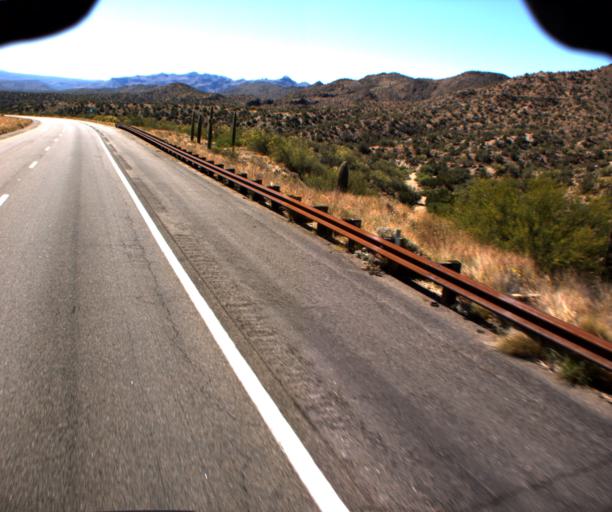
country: US
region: Arizona
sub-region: Yavapai County
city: Bagdad
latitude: 34.4338
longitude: -113.2550
